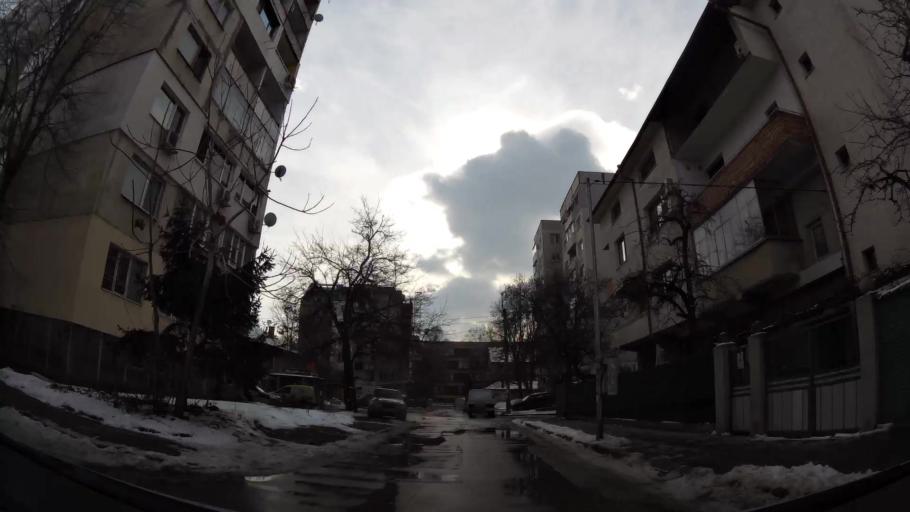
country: BG
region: Sofia-Capital
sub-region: Stolichna Obshtina
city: Sofia
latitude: 42.7083
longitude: 23.3591
